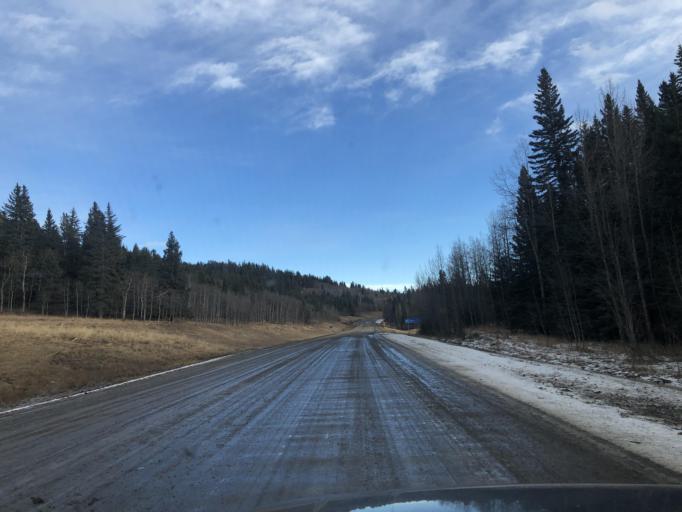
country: CA
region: Alberta
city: Cochrane
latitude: 51.0435
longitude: -114.7604
